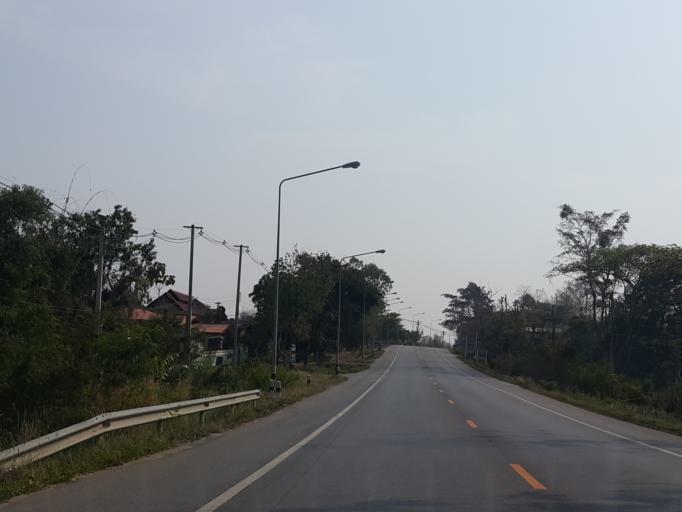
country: TH
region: Lampang
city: Chae Hom
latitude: 18.7172
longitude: 99.5609
